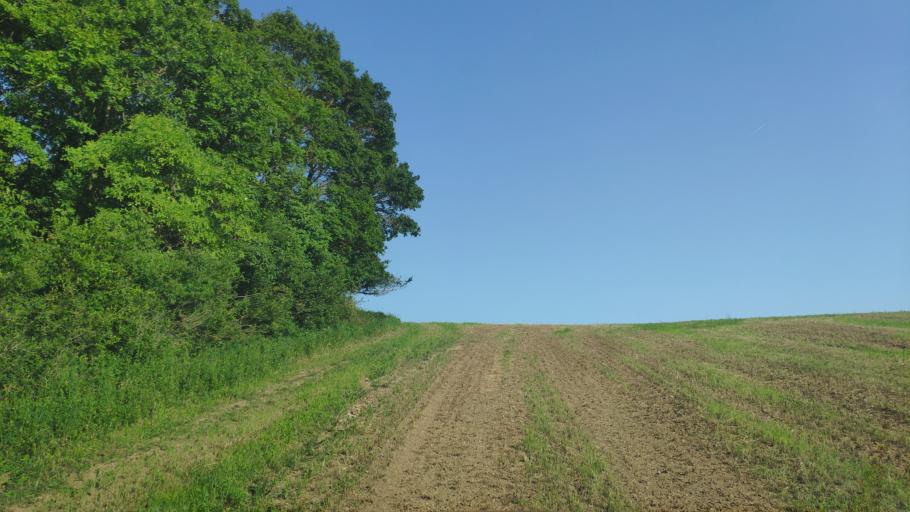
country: SK
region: Kosicky
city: Kosice
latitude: 48.8298
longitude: 21.2246
